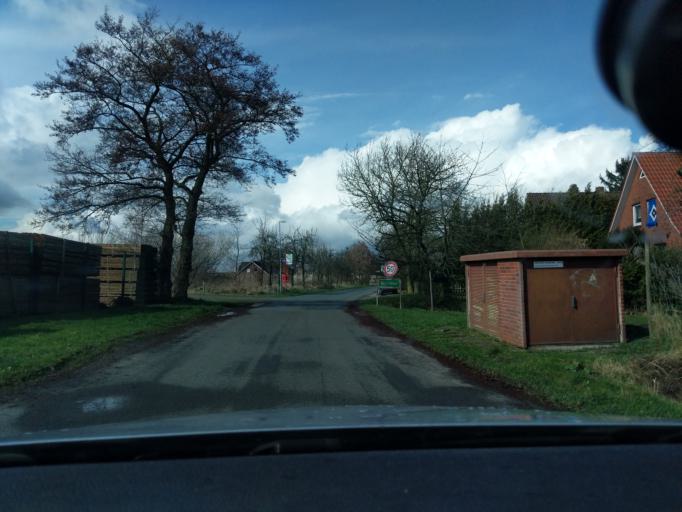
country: DE
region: Lower Saxony
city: Stade
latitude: 53.6075
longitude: 9.5206
